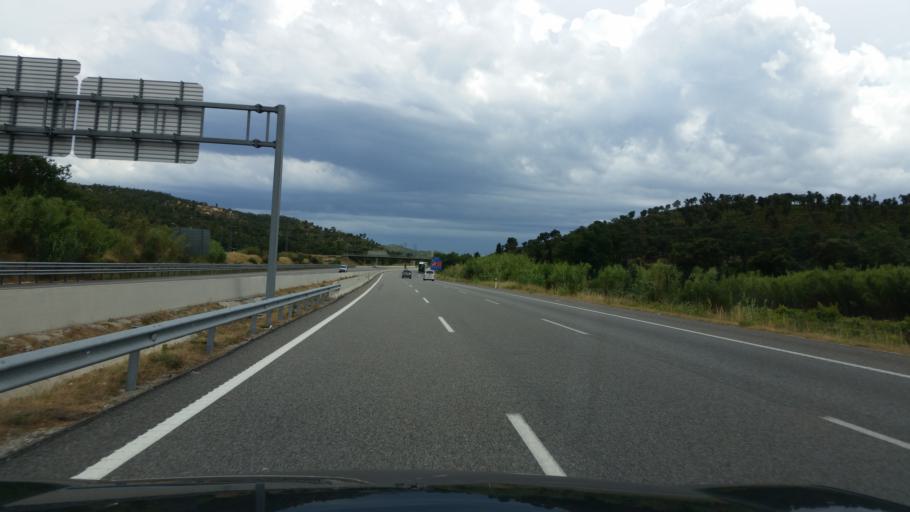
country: ES
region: Catalonia
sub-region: Provincia de Girona
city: la Jonquera
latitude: 42.3937
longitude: 2.8793
